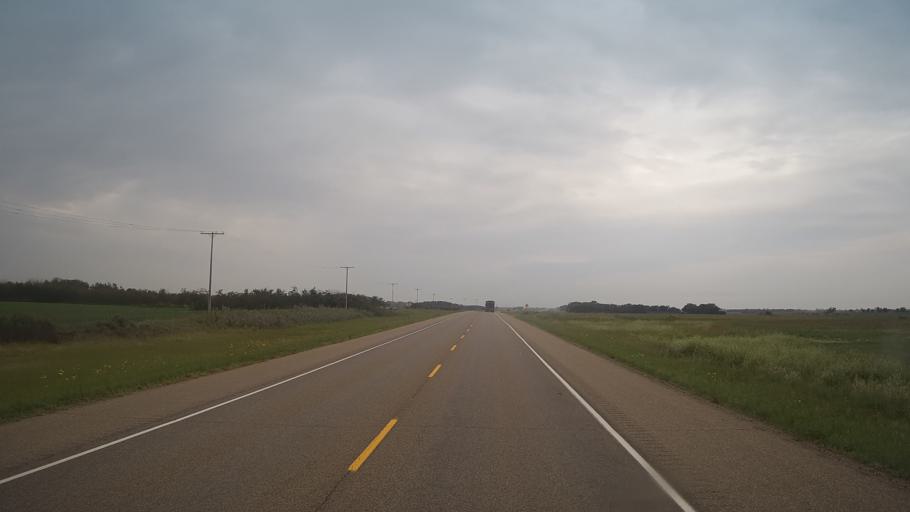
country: CA
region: Saskatchewan
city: Langham
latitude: 52.1292
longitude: -107.1080
